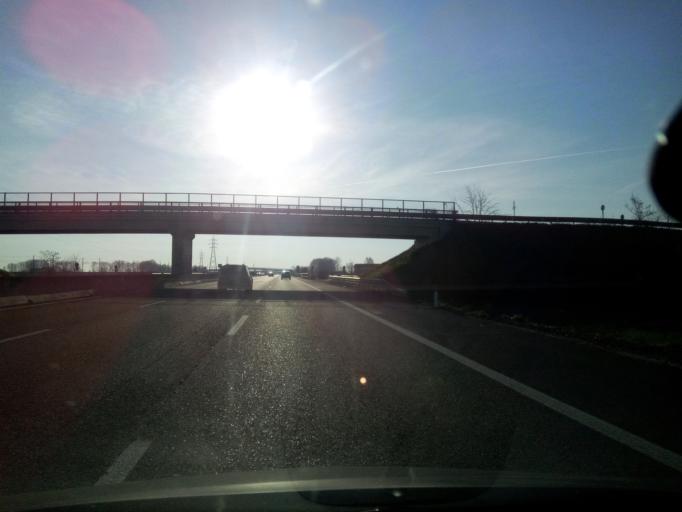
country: IT
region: Emilia-Romagna
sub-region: Provincia di Parma
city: Soragna
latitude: 44.8874
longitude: 10.1014
